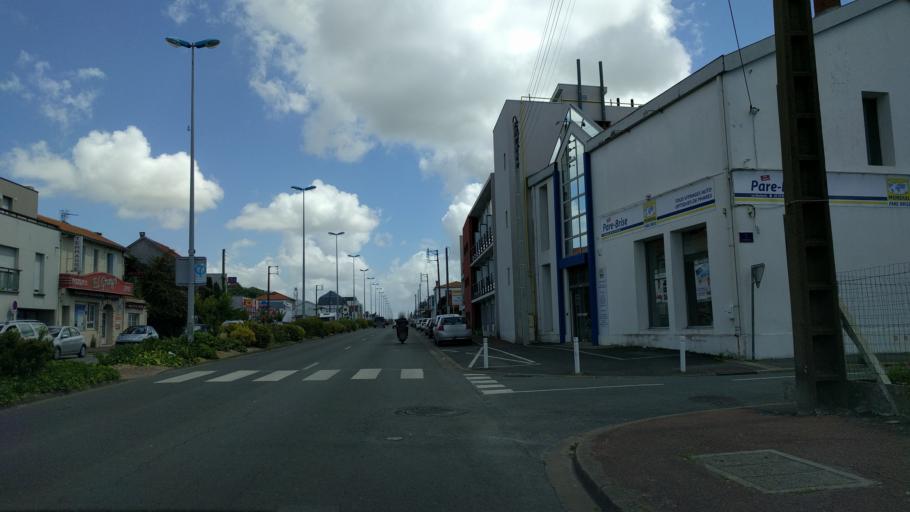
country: FR
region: Poitou-Charentes
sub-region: Departement de la Charente-Maritime
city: La Rochelle
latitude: 46.1684
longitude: -1.1313
